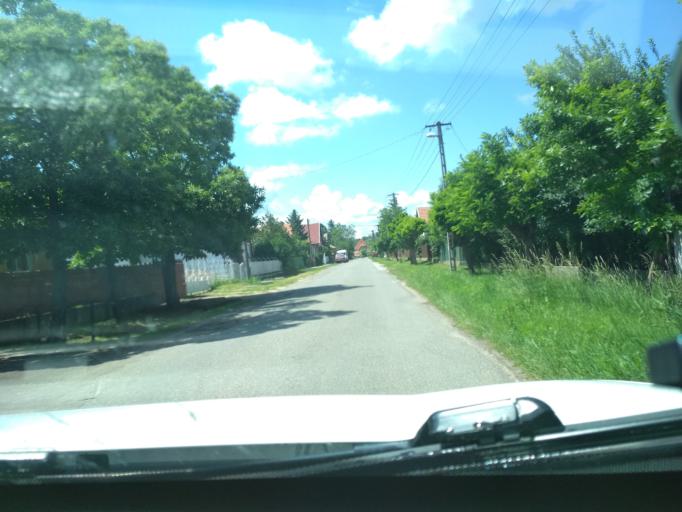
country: HU
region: Jasz-Nagykun-Szolnok
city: Abadszalok
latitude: 47.4821
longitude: 20.6036
